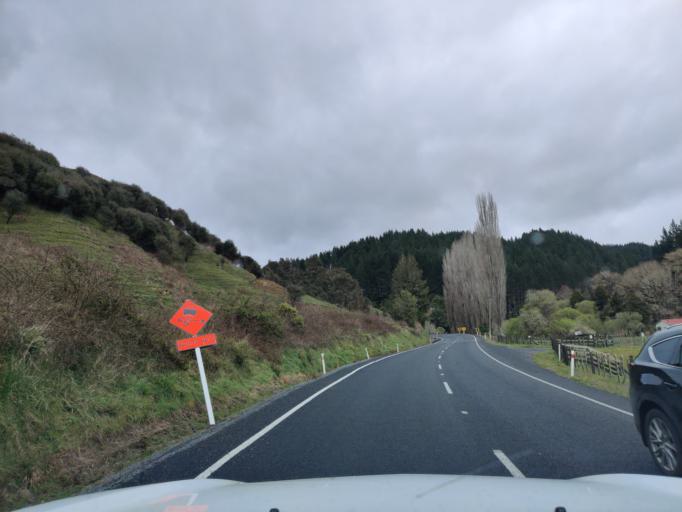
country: NZ
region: Waikato
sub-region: Otorohanga District
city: Otorohanga
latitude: -38.6497
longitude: 175.2107
